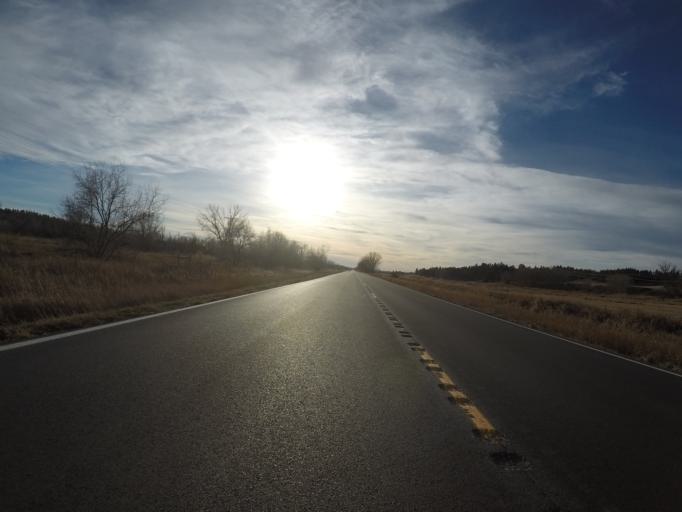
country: US
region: Montana
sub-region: Musselshell County
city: Roundup
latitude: 46.3887
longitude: -108.6185
